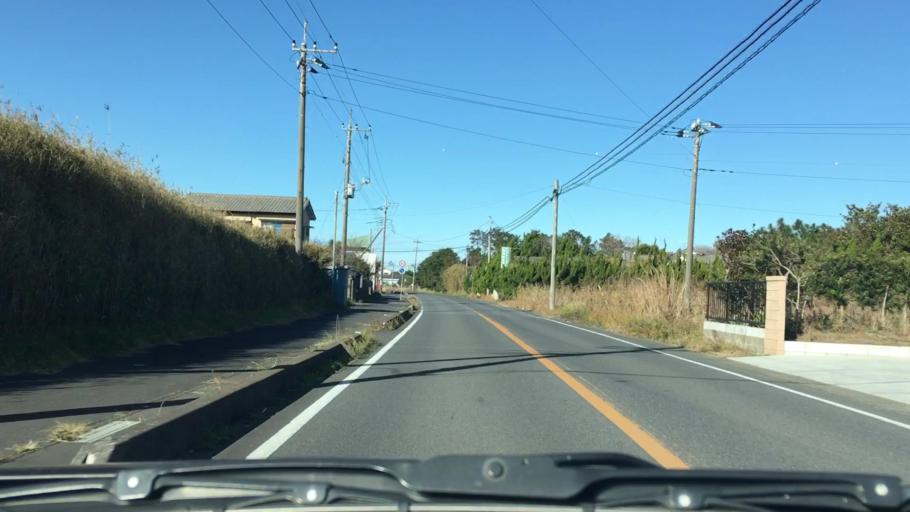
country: JP
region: Chiba
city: Omigawa
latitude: 35.8597
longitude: 140.6931
